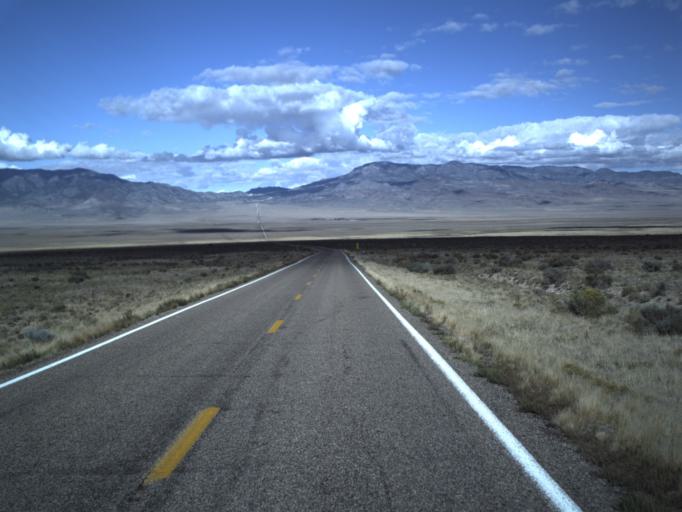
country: US
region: Utah
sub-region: Beaver County
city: Milford
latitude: 38.4414
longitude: -113.3193
